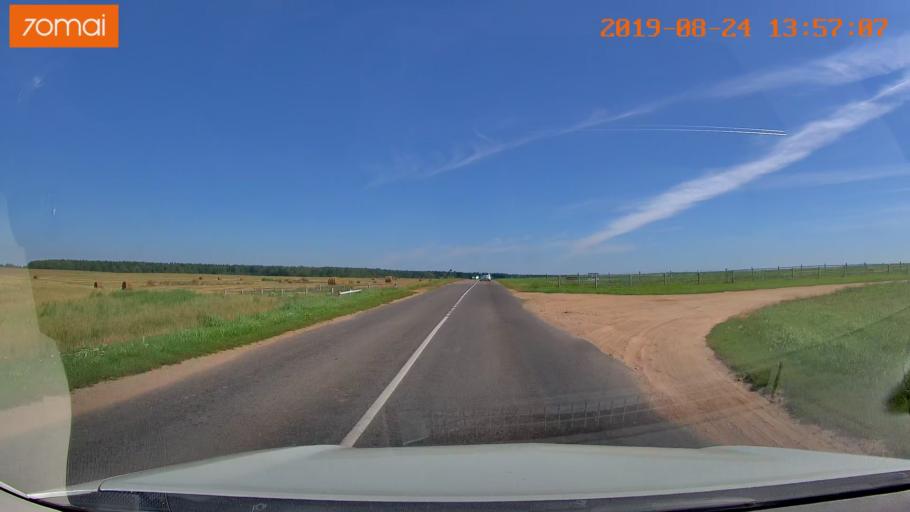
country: BY
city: Michanovichi
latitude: 53.6086
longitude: 27.6509
